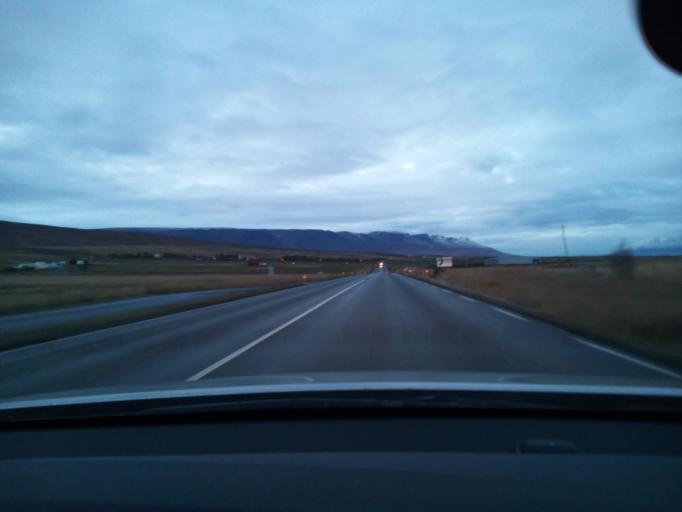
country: IS
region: Northeast
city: Akureyri
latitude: 65.7100
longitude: -18.1618
